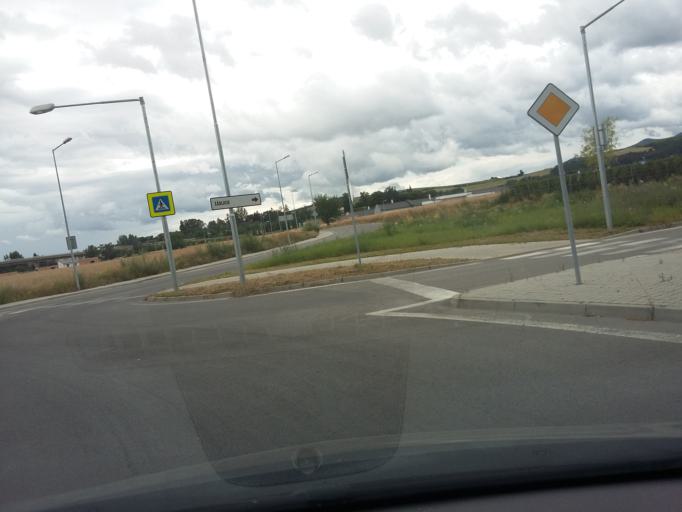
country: SK
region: Trenciansky
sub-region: Okres Trencin
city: Trencin
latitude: 48.9000
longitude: 18.0051
